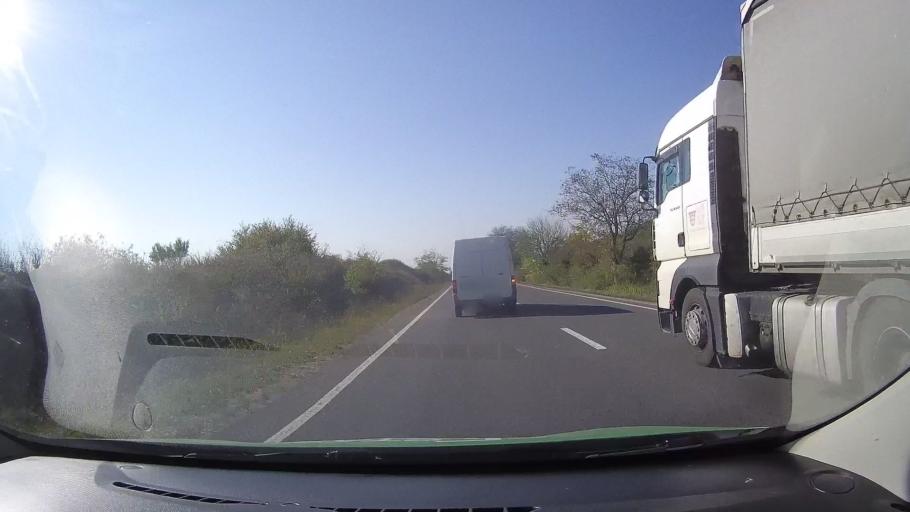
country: RO
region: Satu Mare
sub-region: Comuna Petresti
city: Petresti
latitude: 47.6316
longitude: 22.3945
